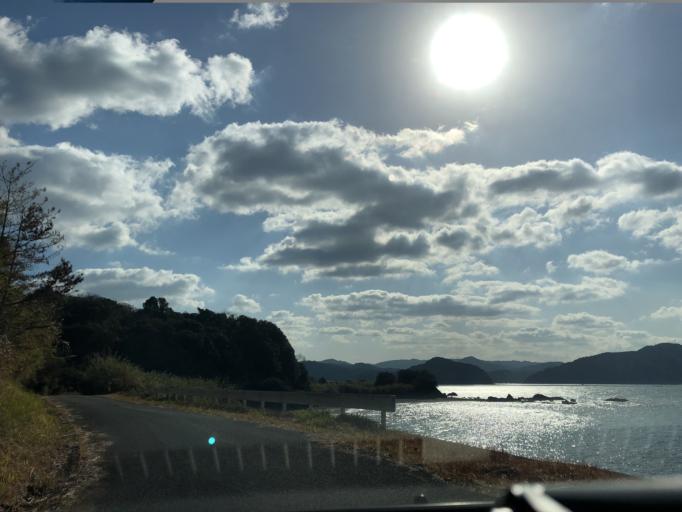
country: JP
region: Kochi
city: Sukumo
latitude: 32.9127
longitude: 132.6934
